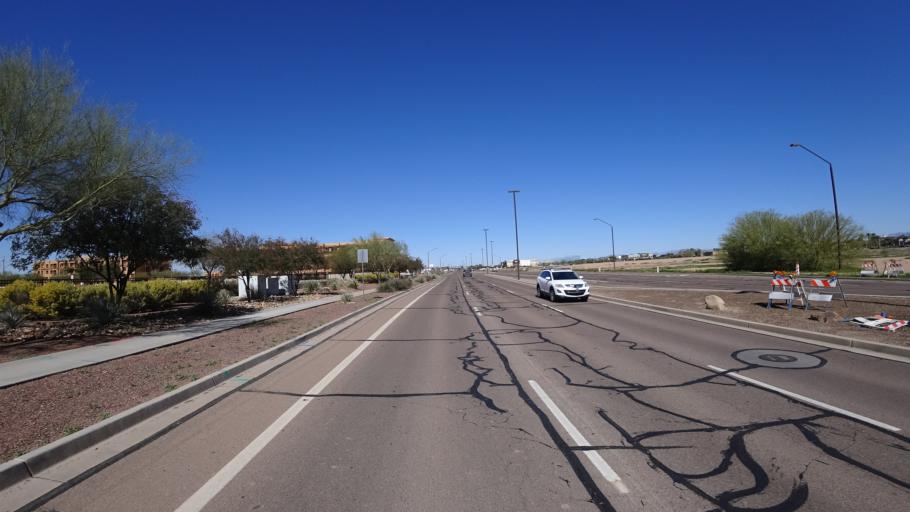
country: US
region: Arizona
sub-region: Maricopa County
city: Gilbert
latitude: 33.3022
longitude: -111.7471
